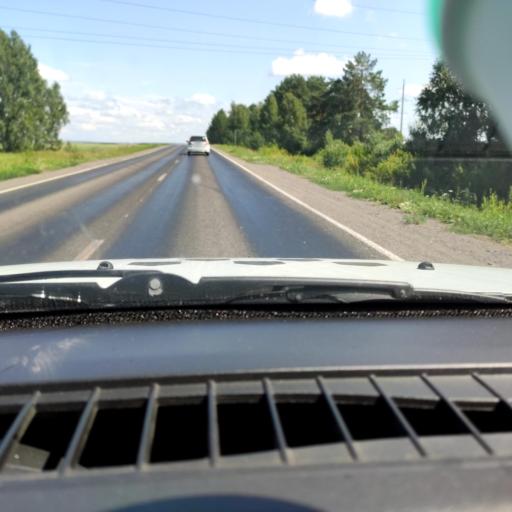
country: RU
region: Bashkortostan
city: Verkhniye Kigi
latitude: 55.4597
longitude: 58.4504
